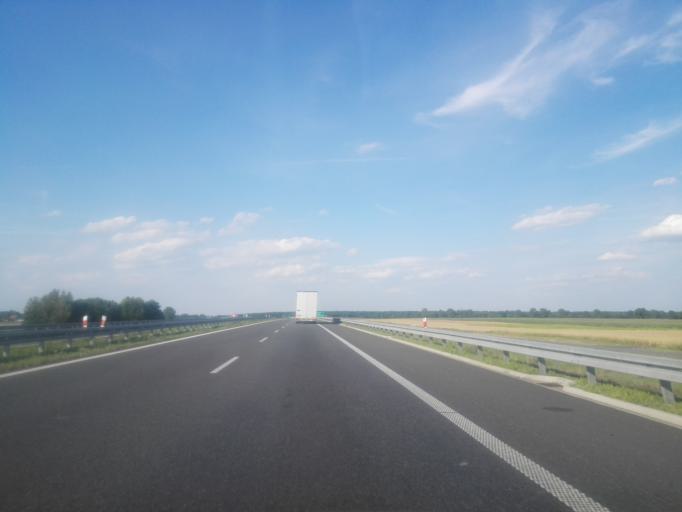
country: PL
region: Lower Silesian Voivodeship
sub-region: Powiat olesnicki
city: Twardogora
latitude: 51.2772
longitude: 17.5626
